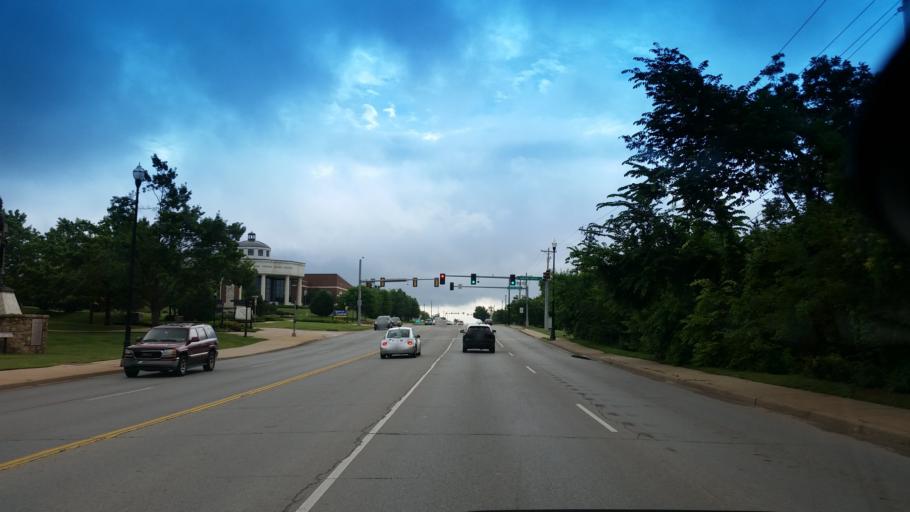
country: US
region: Oklahoma
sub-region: Oklahoma County
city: Edmond
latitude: 35.6528
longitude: -97.4727
